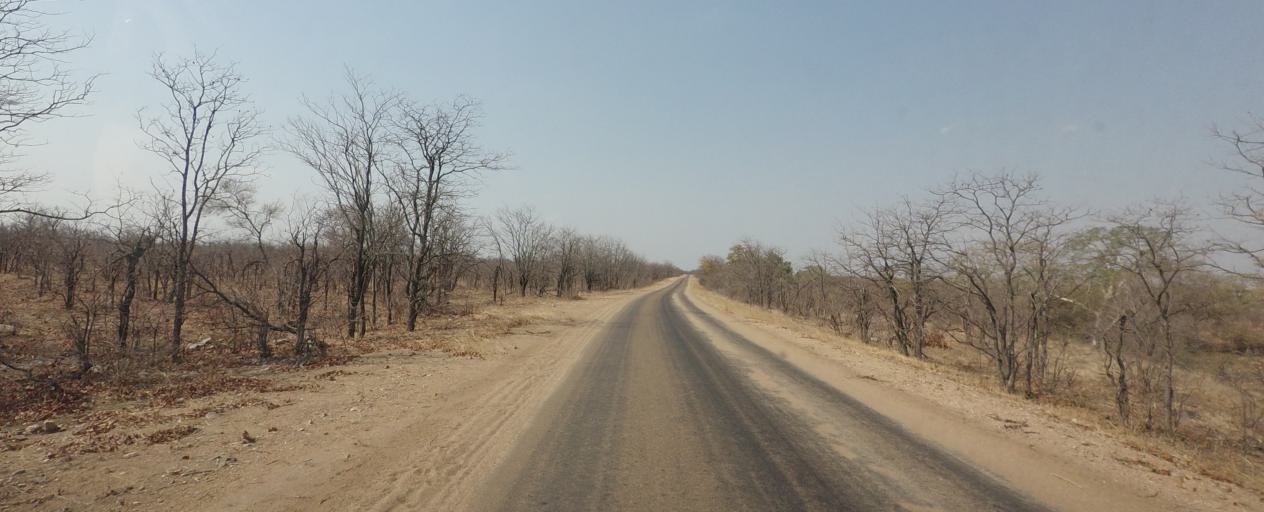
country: ZA
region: Limpopo
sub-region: Mopani District Municipality
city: Giyani
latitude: -23.1978
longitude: 31.3092
